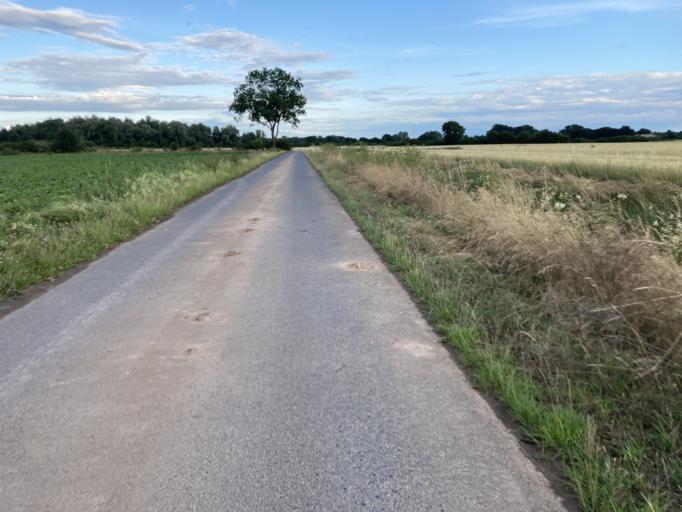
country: DE
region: Lower Saxony
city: Verden
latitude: 52.9096
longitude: 9.1957
